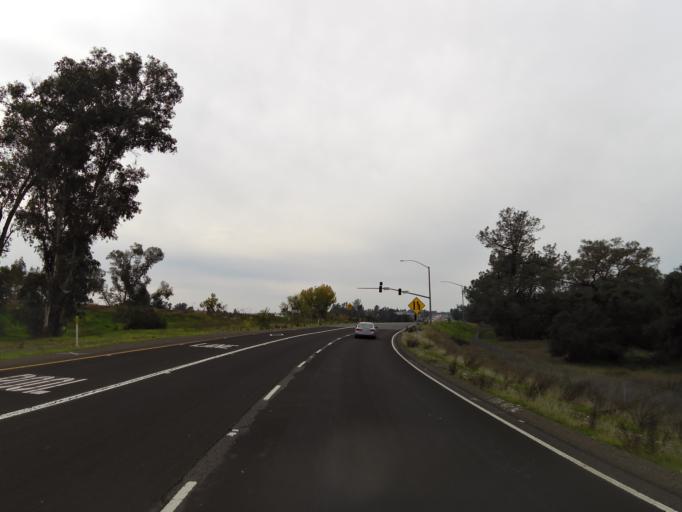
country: US
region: California
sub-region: Sacramento County
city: Folsom
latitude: 38.6404
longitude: -121.1993
